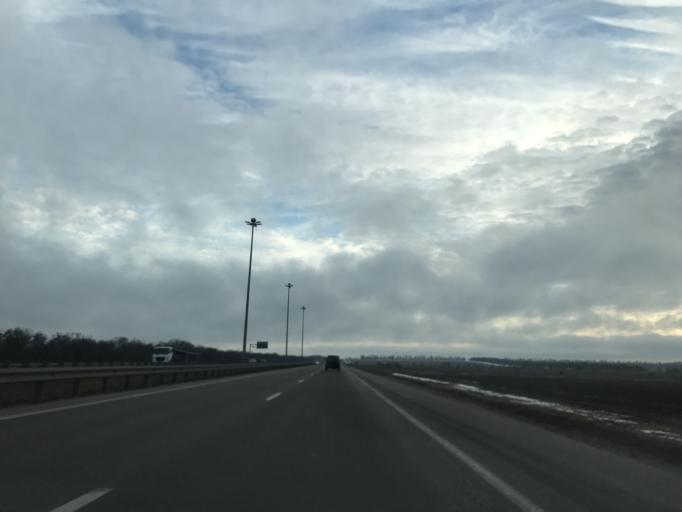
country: RU
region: Rostov
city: Staraya Stanitsa
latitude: 48.3954
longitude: 40.3402
